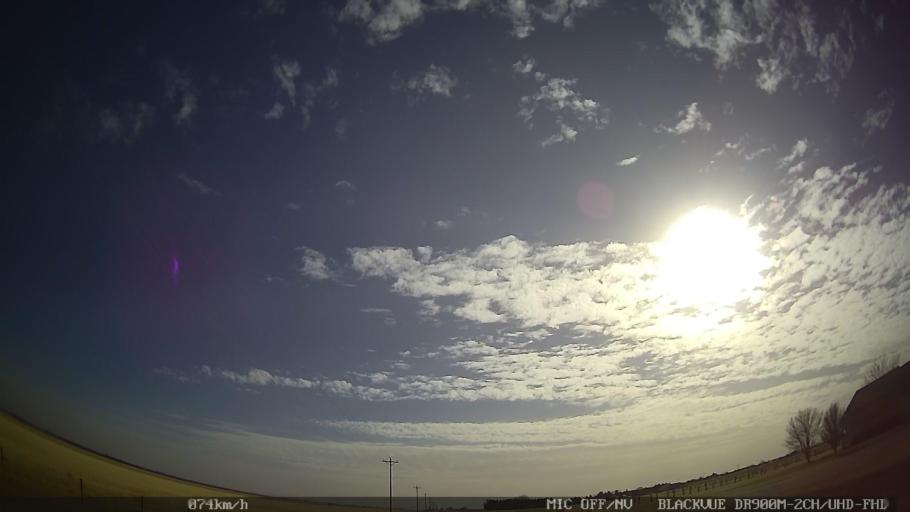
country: US
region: New Mexico
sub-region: Curry County
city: Texico
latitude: 34.4240
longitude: -103.0908
